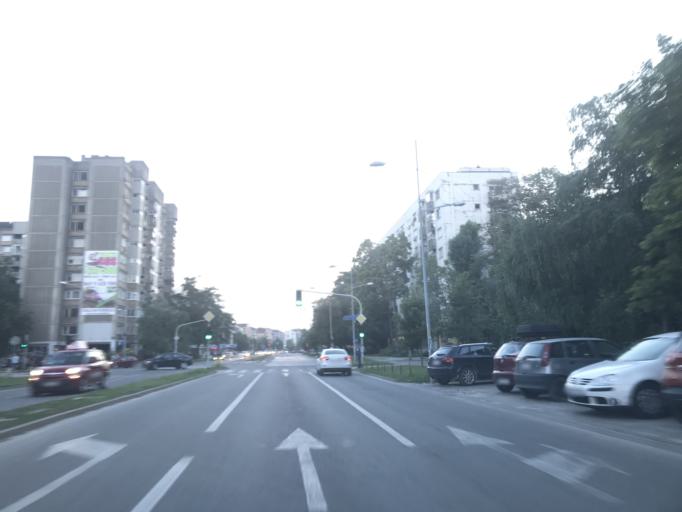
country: RS
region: Autonomna Pokrajina Vojvodina
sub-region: Juznobacki Okrug
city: Novi Sad
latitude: 45.2614
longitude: 19.8346
